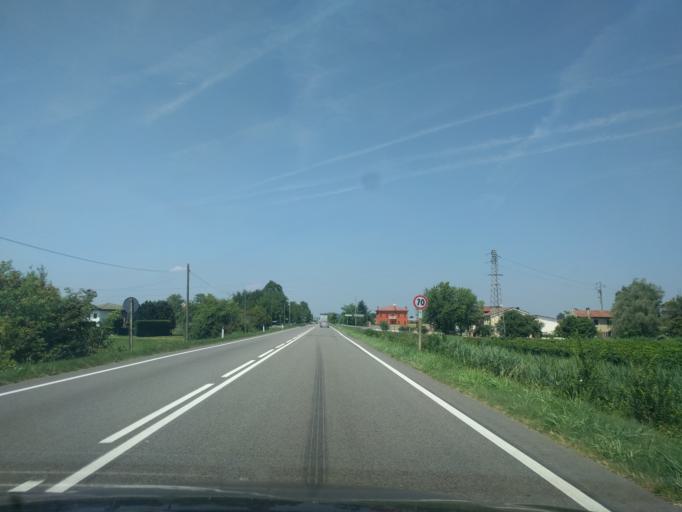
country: IT
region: Veneto
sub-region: Provincia di Padova
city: Solesino
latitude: 45.1680
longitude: 11.7568
